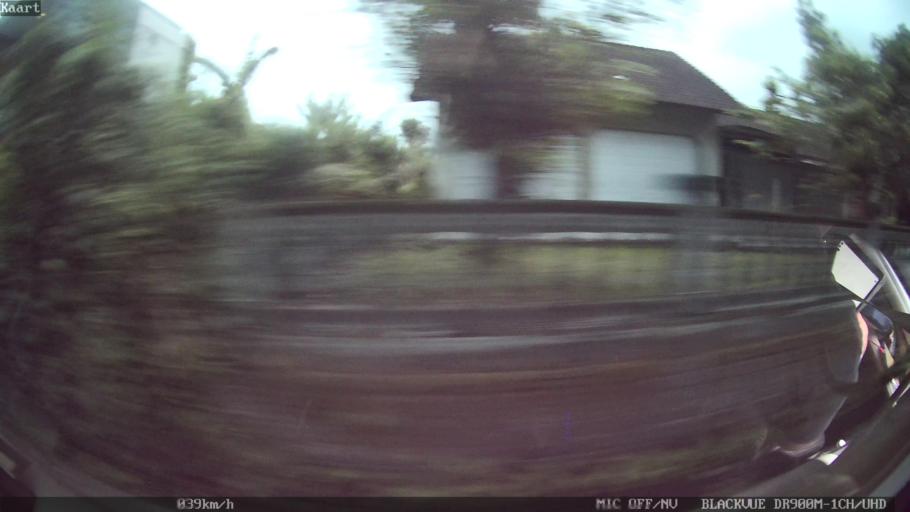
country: ID
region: Bali
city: Banjar Pasekan
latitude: -8.6176
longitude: 115.2710
